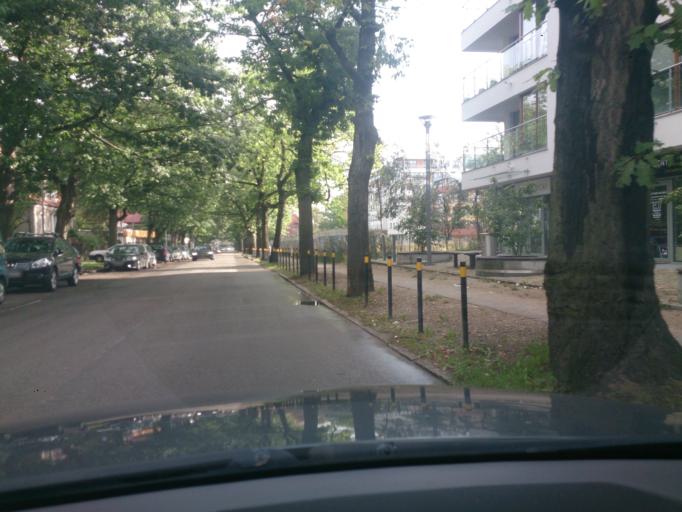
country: PL
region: Pomeranian Voivodeship
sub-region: Sopot
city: Sopot
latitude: 54.3839
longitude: 18.5884
